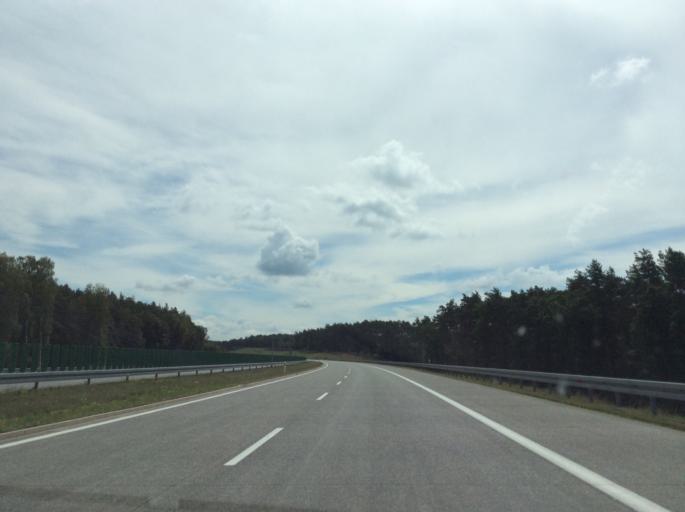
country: PL
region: Lubusz
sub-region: Powiat swiebodzinski
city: Lagow
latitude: 52.2974
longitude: 15.2644
